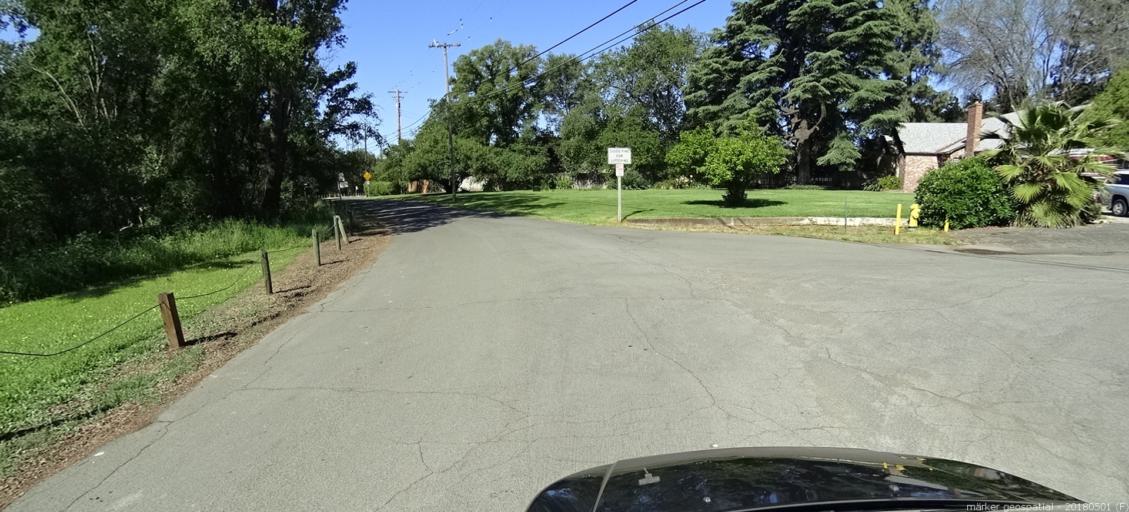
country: US
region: California
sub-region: Sacramento County
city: Foothill Farms
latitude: 38.6446
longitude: -121.3721
